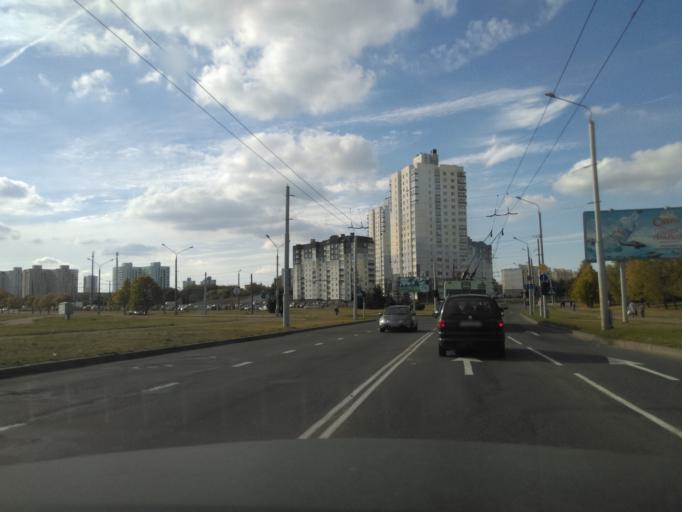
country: BY
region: Minsk
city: Hatava
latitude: 53.8563
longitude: 27.6317
